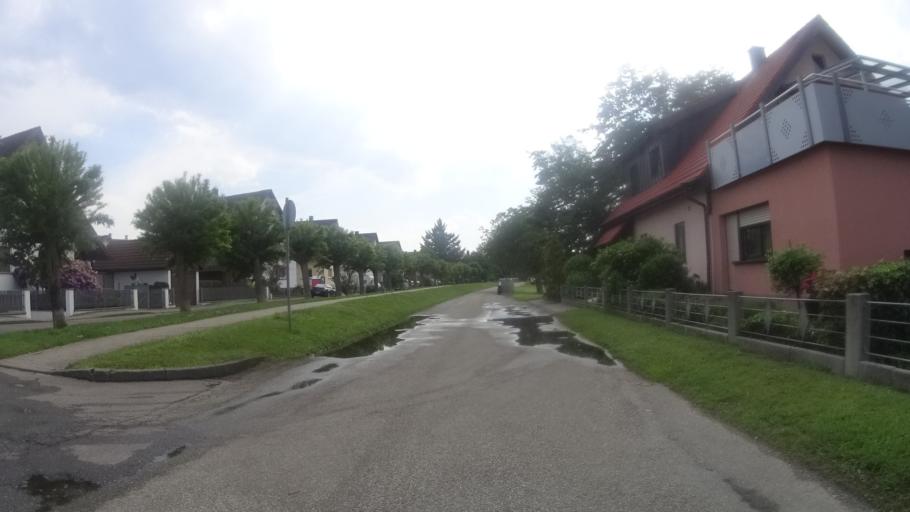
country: DE
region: Baden-Wuerttemberg
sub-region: Karlsruhe Region
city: Iffezheim
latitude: 48.8228
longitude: 8.1497
